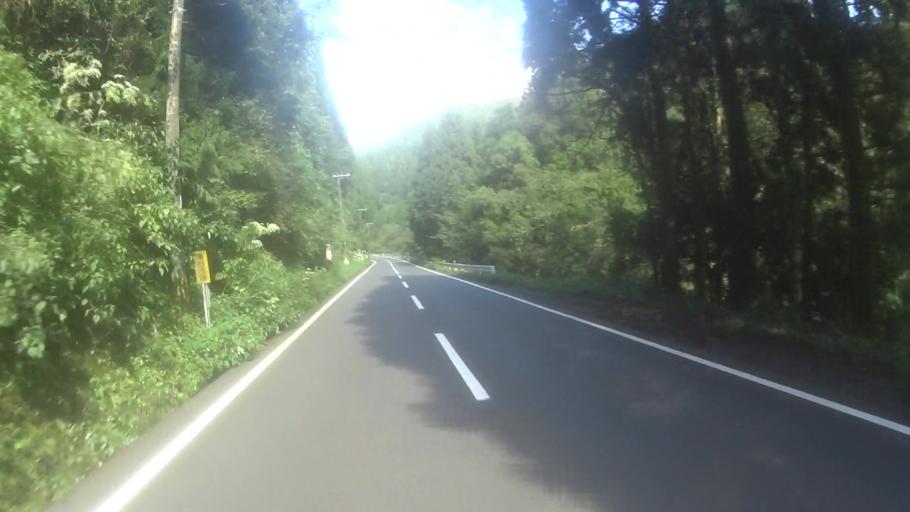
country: JP
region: Kyoto
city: Miyazu
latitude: 35.6427
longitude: 135.1295
